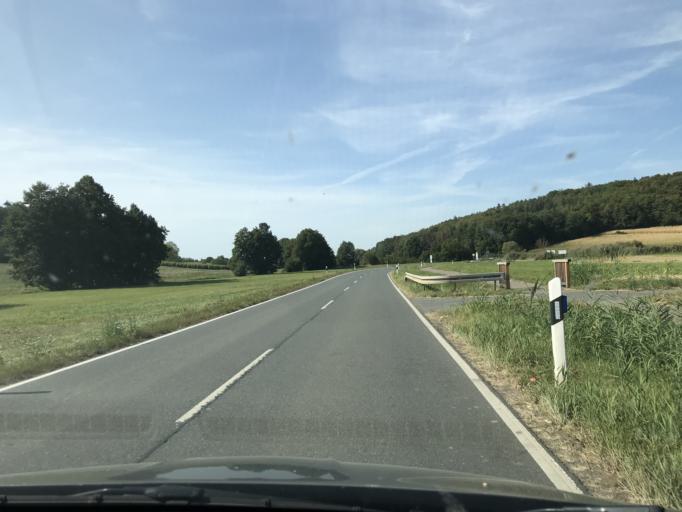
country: DE
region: Hesse
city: Gross-Umstadt
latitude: 49.8427
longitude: 8.9456
